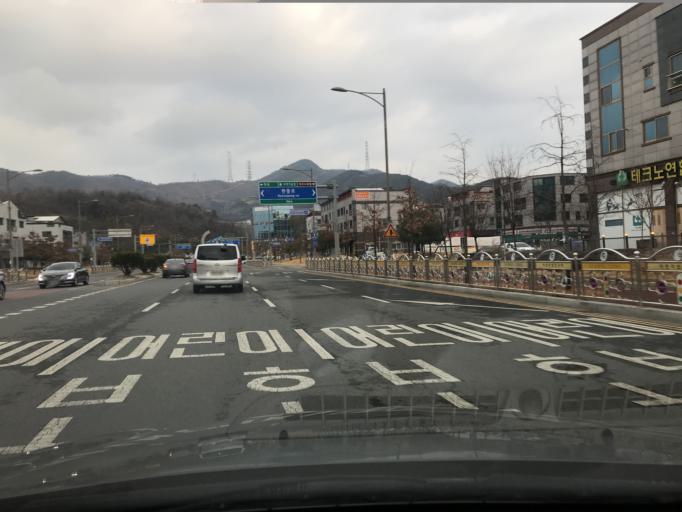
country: KR
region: Daegu
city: Hwawon
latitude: 35.6970
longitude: 128.4578
